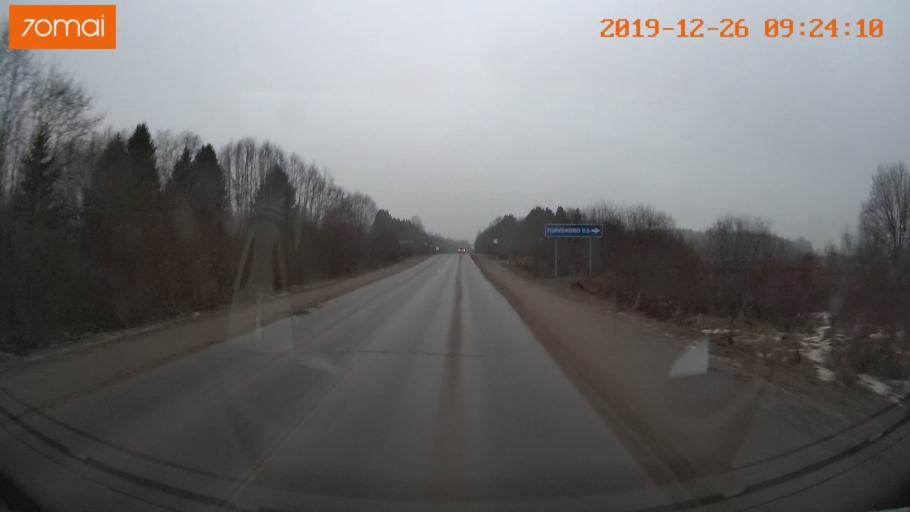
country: RU
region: Vologda
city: Gryazovets
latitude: 58.9976
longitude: 40.2016
